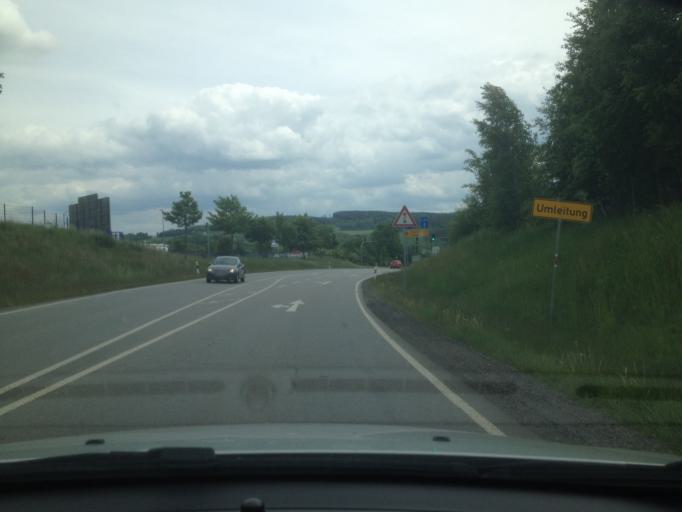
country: DE
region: Saxony
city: Stollberg
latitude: 50.7002
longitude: 12.7655
